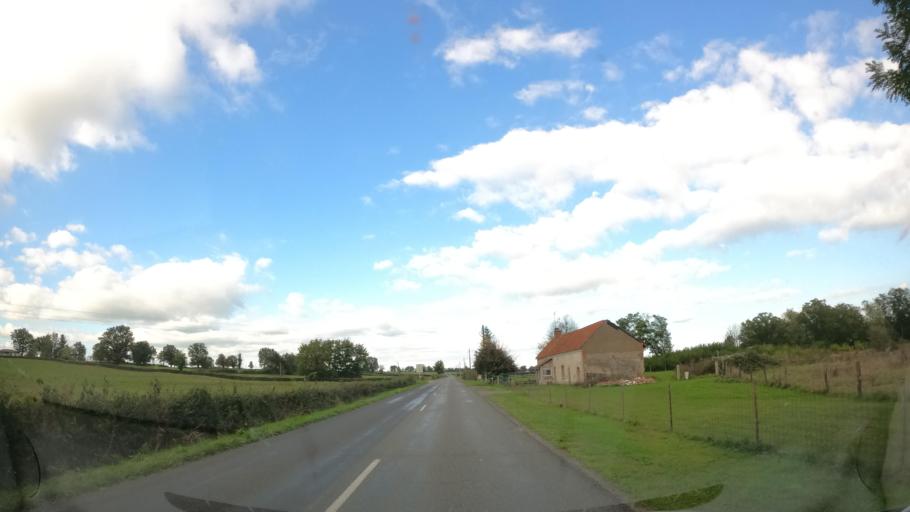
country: FR
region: Auvergne
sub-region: Departement de l'Allier
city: Dompierre-sur-Besbre
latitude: 46.4910
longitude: 3.6583
